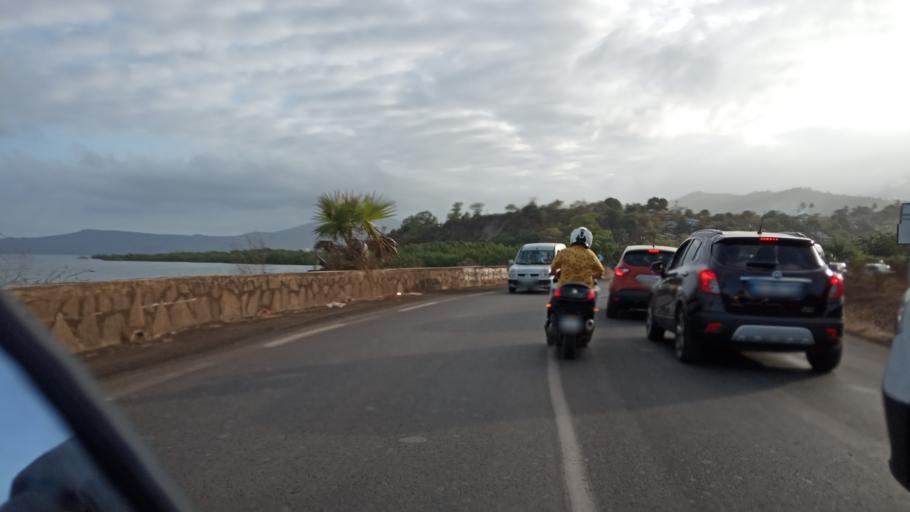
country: YT
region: Mamoudzou
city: Mamoudzou
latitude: -12.7944
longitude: 45.2183
